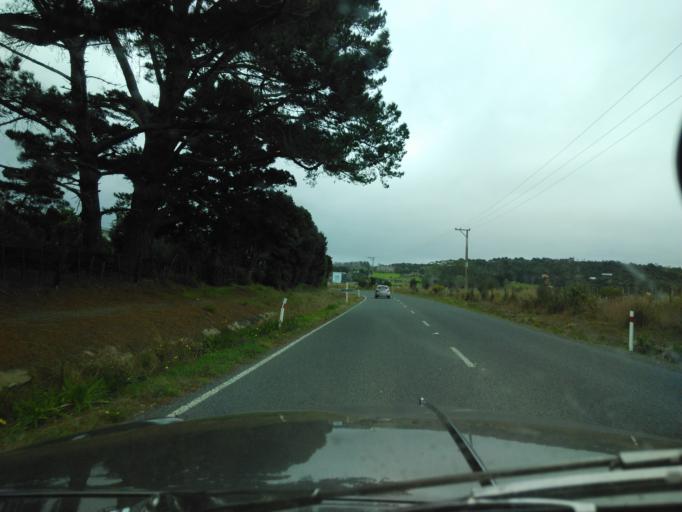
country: NZ
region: Auckland
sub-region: Auckland
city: Wellsford
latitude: -36.1110
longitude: 174.5766
